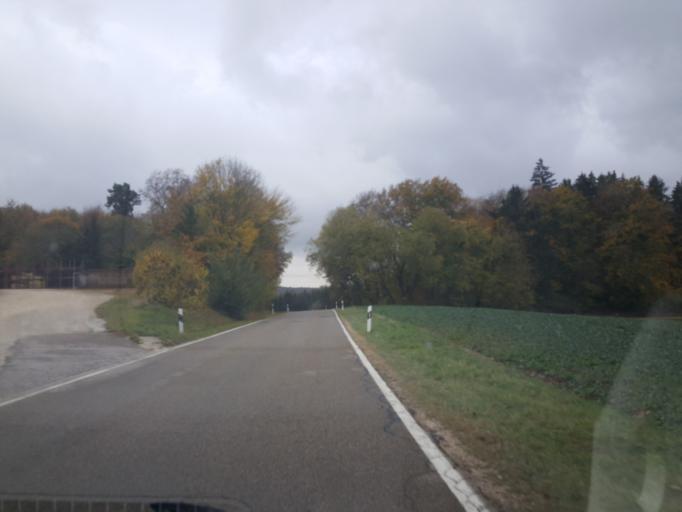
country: DE
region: Bavaria
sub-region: Upper Bavaria
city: Rennertshofen
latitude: 48.8010
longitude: 11.0576
